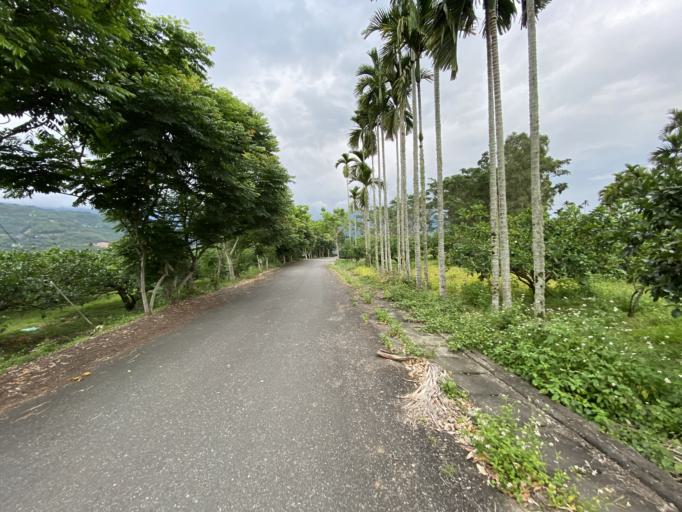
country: TW
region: Taiwan
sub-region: Hualien
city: Hualian
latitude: 23.4699
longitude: 121.3594
